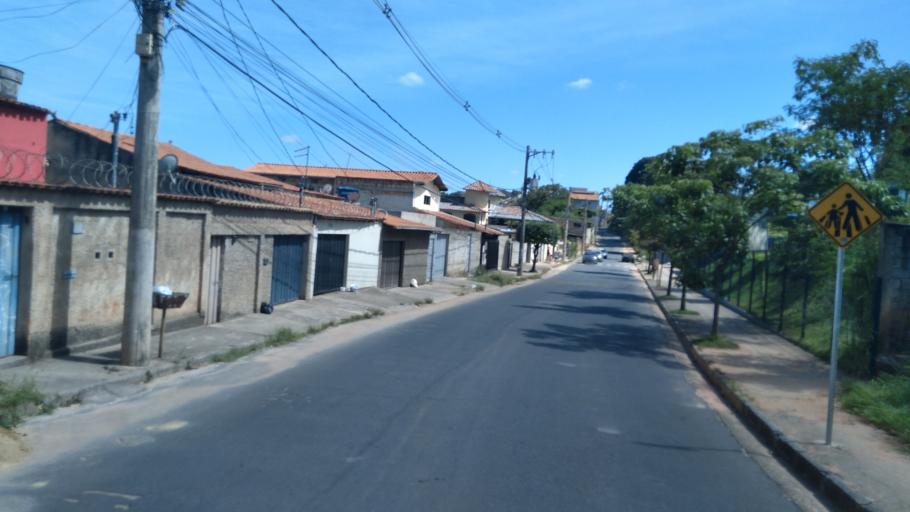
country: BR
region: Minas Gerais
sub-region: Belo Horizonte
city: Belo Horizonte
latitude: -19.8470
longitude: -43.9008
